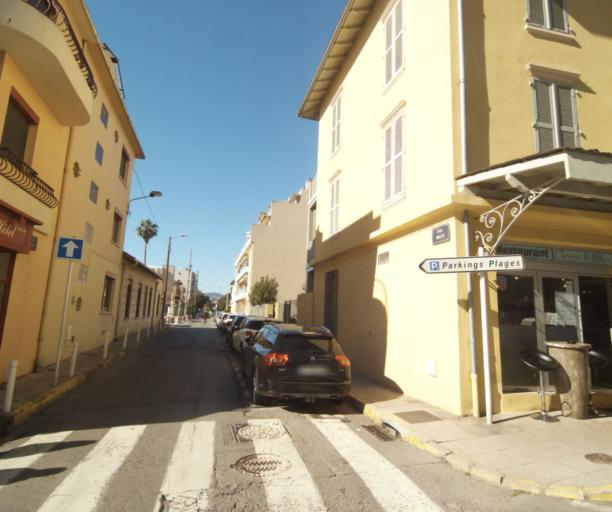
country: FR
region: Provence-Alpes-Cote d'Azur
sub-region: Departement des Alpes-Maritimes
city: Antibes
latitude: 43.5717
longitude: 7.1025
